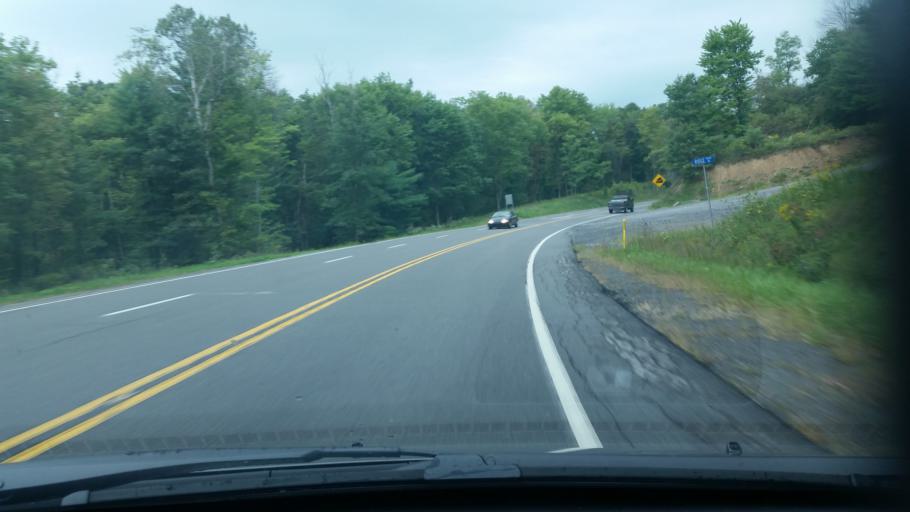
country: US
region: Pennsylvania
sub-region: Clearfield County
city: Shiloh
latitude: 41.0651
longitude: -78.3146
